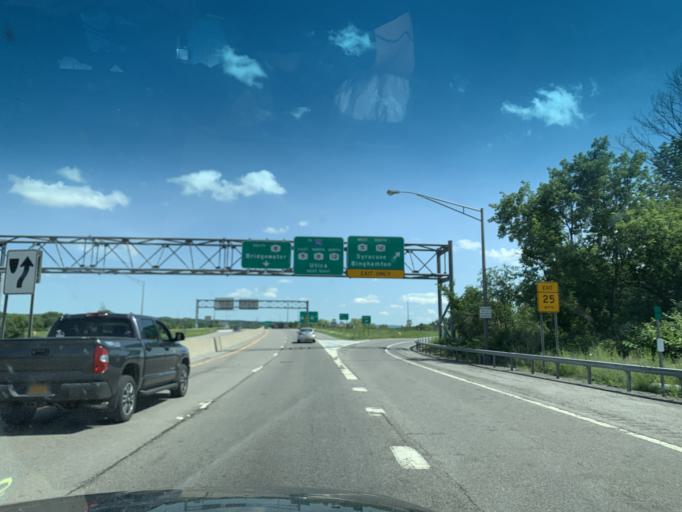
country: US
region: New York
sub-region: Oneida County
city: New Hartford
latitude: 43.0821
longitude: -75.2948
